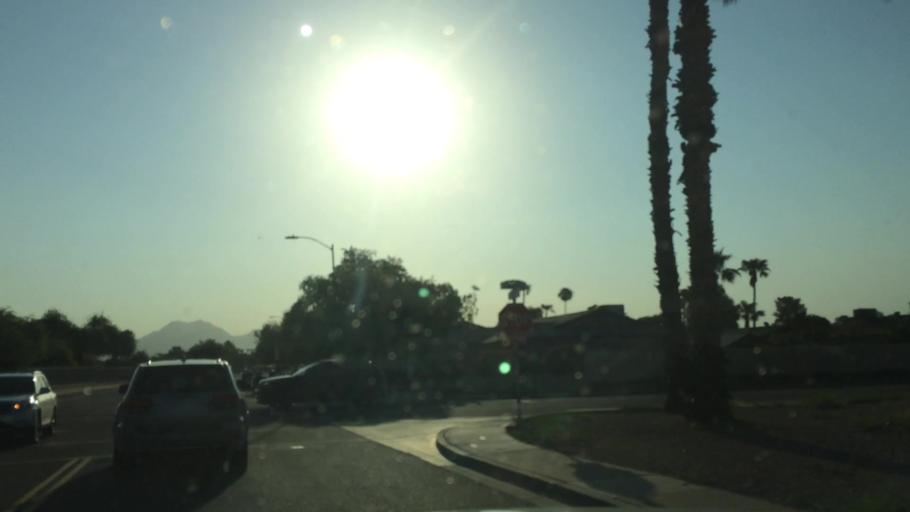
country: US
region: Arizona
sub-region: Maricopa County
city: Paradise Valley
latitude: 33.6195
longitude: -111.9531
